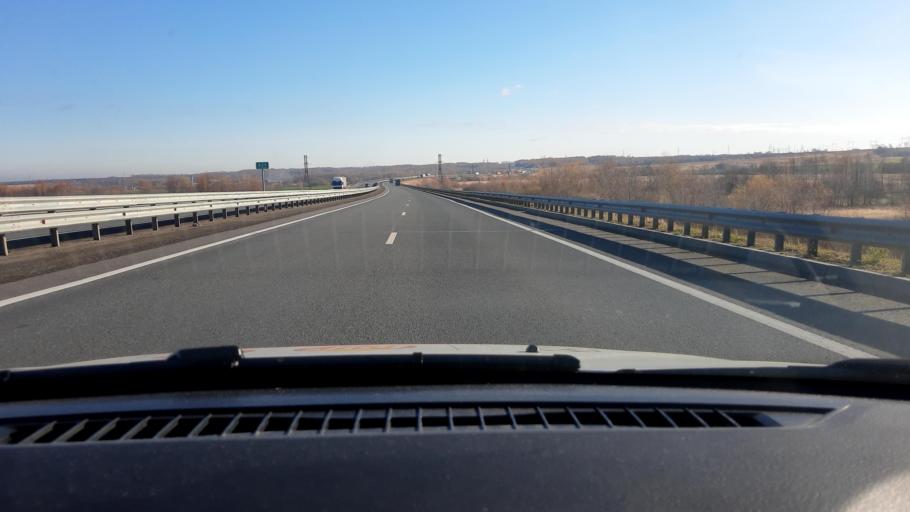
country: RU
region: Nizjnij Novgorod
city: Burevestnik
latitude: 56.1138
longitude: 43.8420
